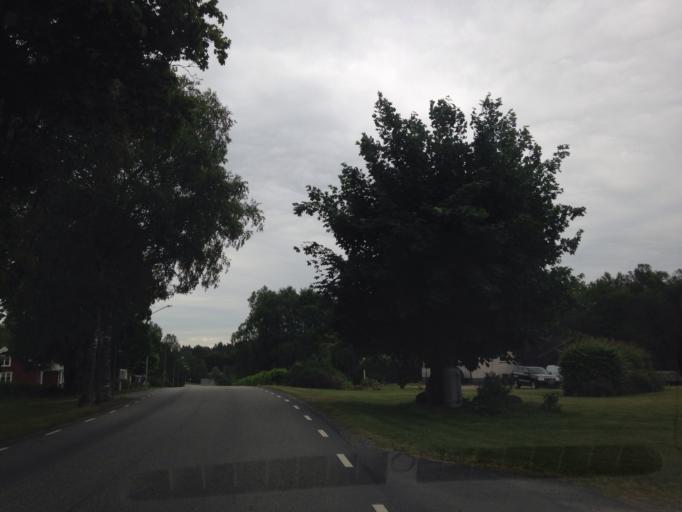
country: SE
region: Vaestra Goetaland
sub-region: Marks Kommun
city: Horred
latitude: 57.4712
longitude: 12.4803
